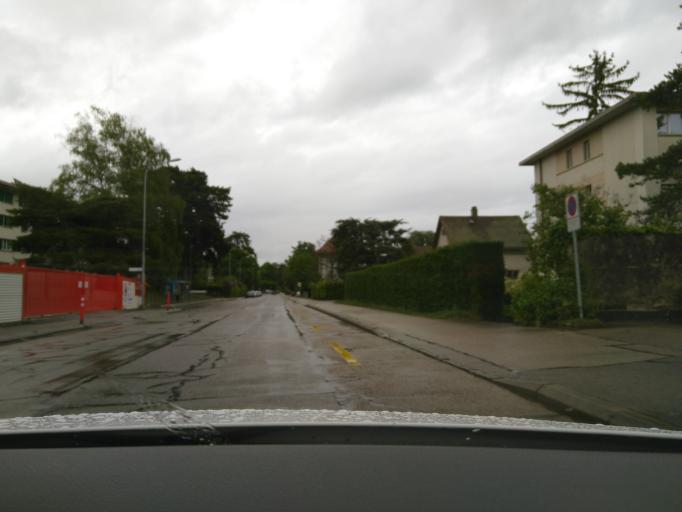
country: CH
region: Vaud
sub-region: Nyon District
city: Nyon
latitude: 46.3824
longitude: 6.2297
